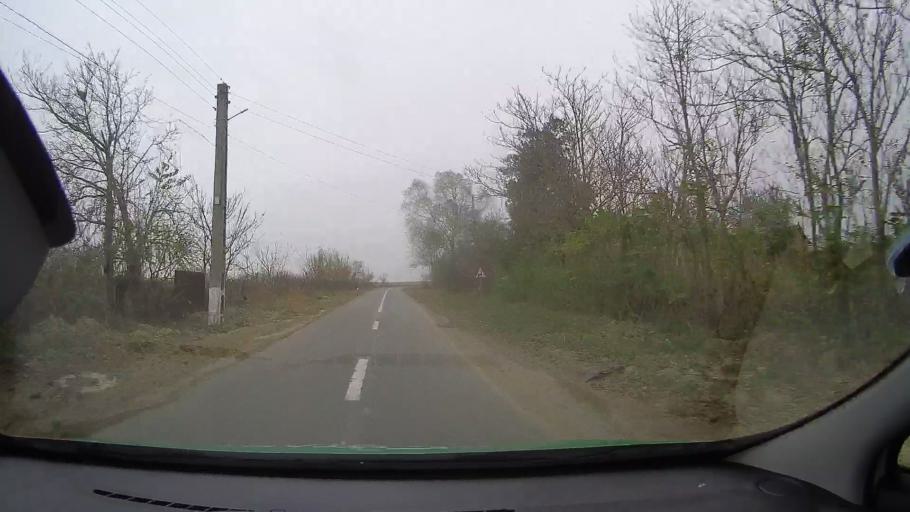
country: RO
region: Constanta
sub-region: Comuna Vulturu
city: Vulturu
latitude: 44.6557
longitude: 28.2669
